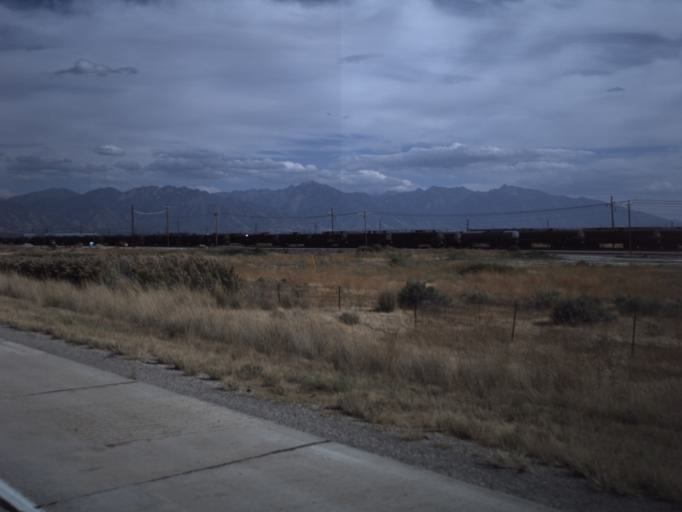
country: US
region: Utah
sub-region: Salt Lake County
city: Magna
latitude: 40.7709
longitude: -112.0471
